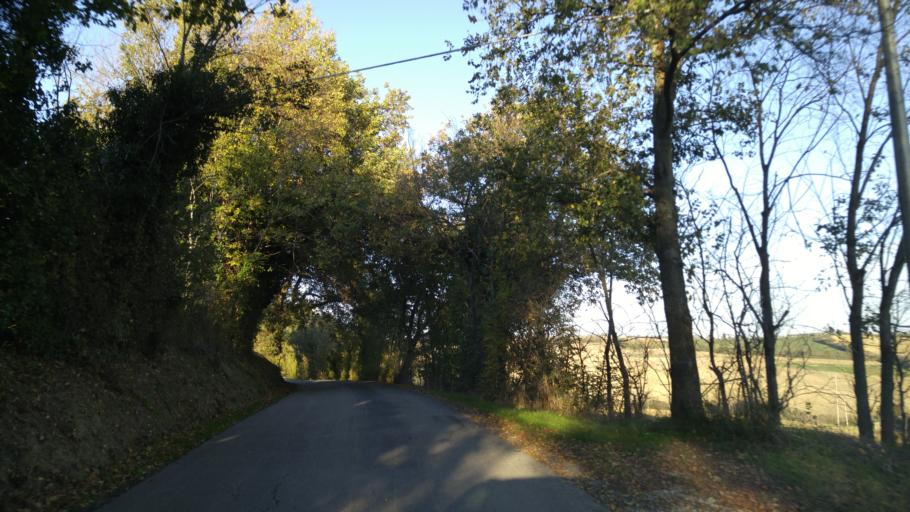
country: IT
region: The Marches
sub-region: Provincia di Pesaro e Urbino
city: Cartoceto
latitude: 43.7942
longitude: 12.9004
